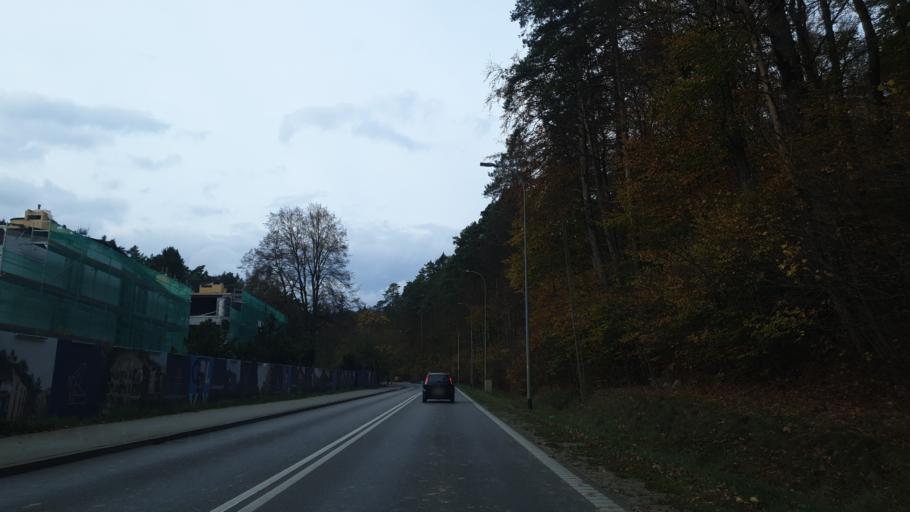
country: PL
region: Pomeranian Voivodeship
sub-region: Sopot
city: Sopot
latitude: 54.4128
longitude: 18.5473
